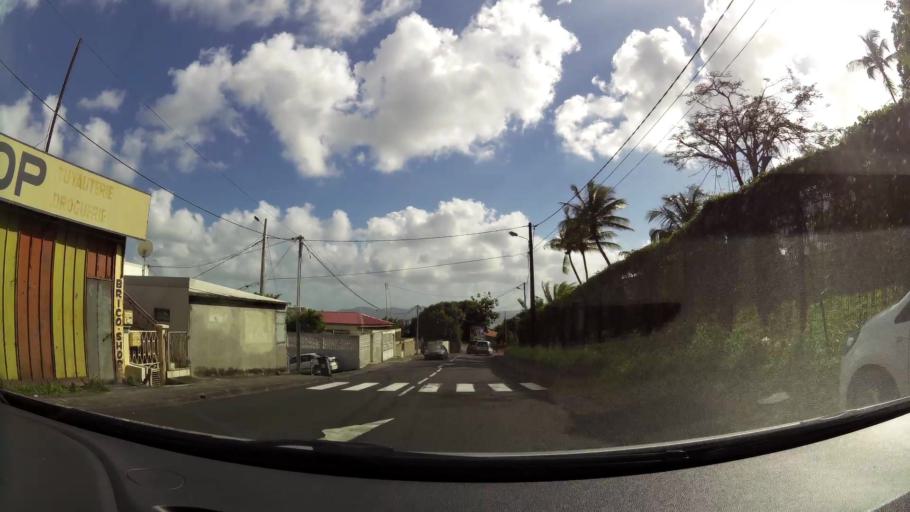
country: MQ
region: Martinique
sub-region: Martinique
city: Fort-de-France
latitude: 14.6167
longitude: -61.0618
